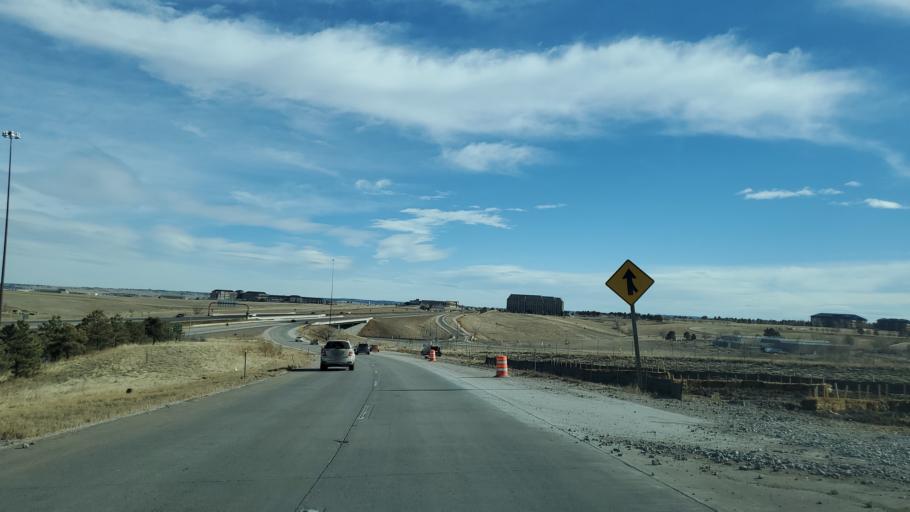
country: US
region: Colorado
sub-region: Douglas County
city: Meridian
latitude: 39.5546
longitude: -104.8675
